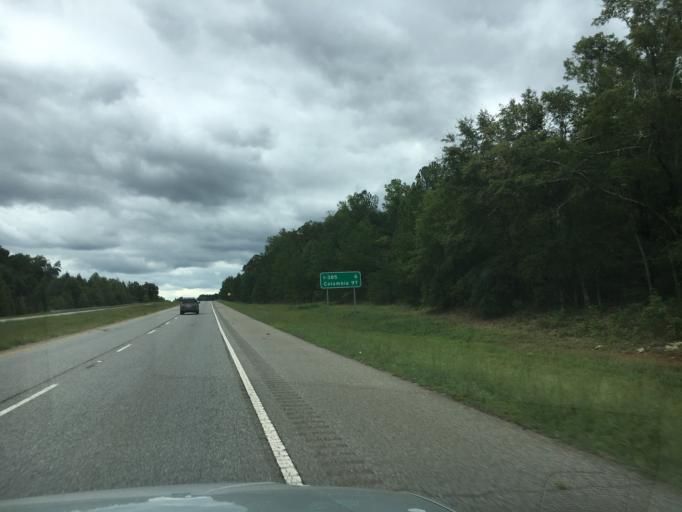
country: US
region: South Carolina
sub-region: Greenville County
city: Golden Grove
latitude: 34.7217
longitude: -82.3717
